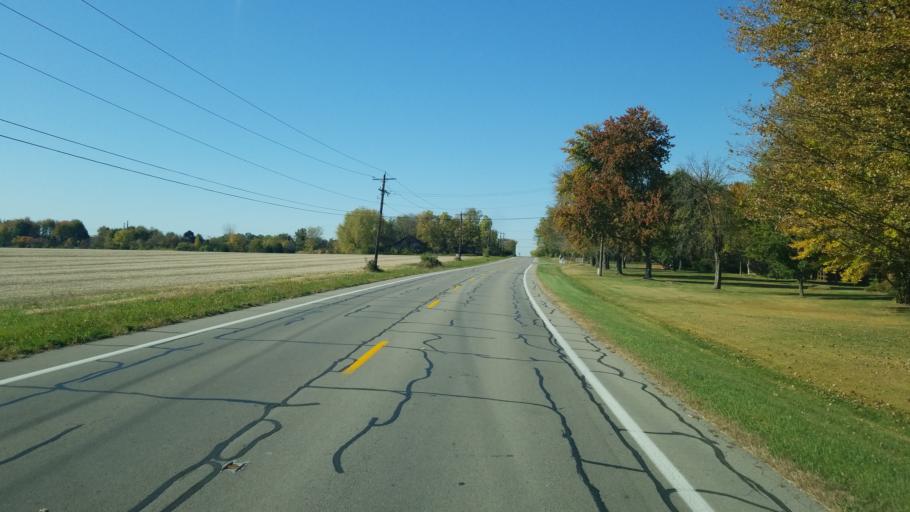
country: US
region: Ohio
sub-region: Warren County
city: Morrow
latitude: 39.3669
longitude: -84.0686
